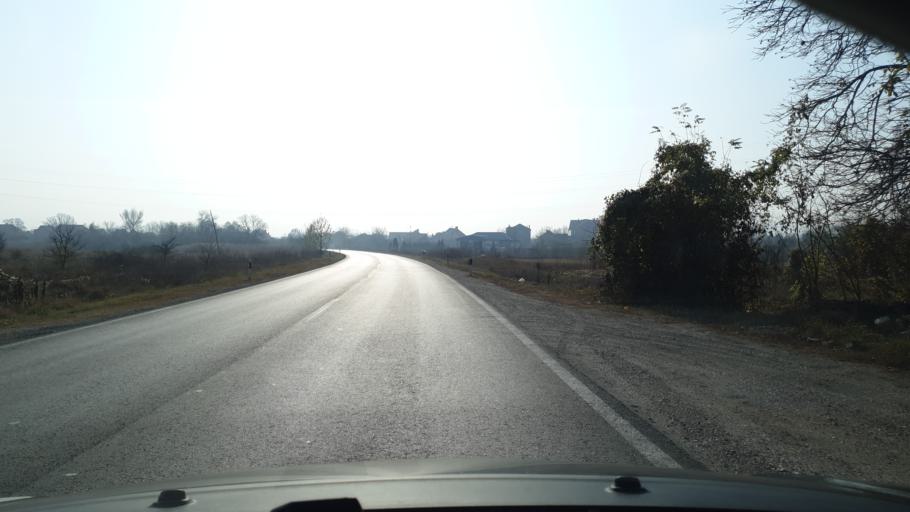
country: RS
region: Central Serbia
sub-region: Zajecarski Okrug
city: Zajecar
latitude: 43.9157
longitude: 22.2947
